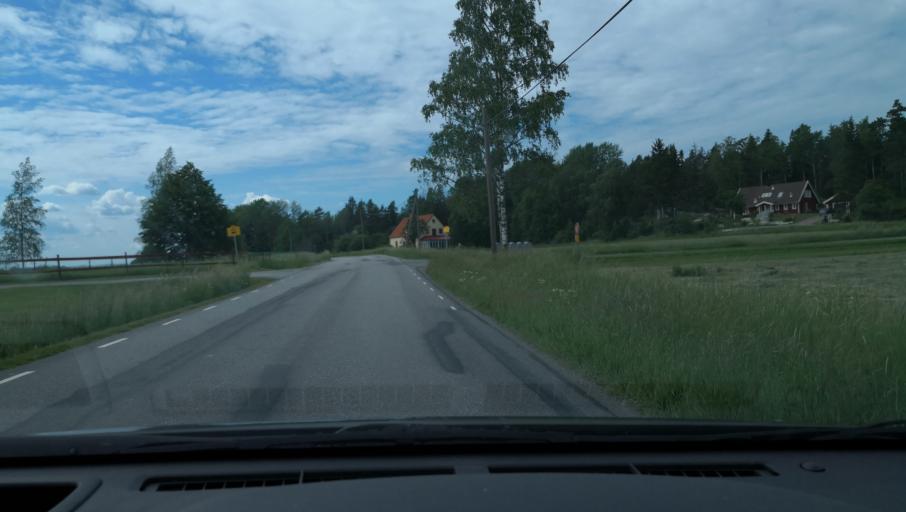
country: SE
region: Uppsala
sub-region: Uppsala Kommun
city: Uppsala
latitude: 59.8090
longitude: 17.5205
